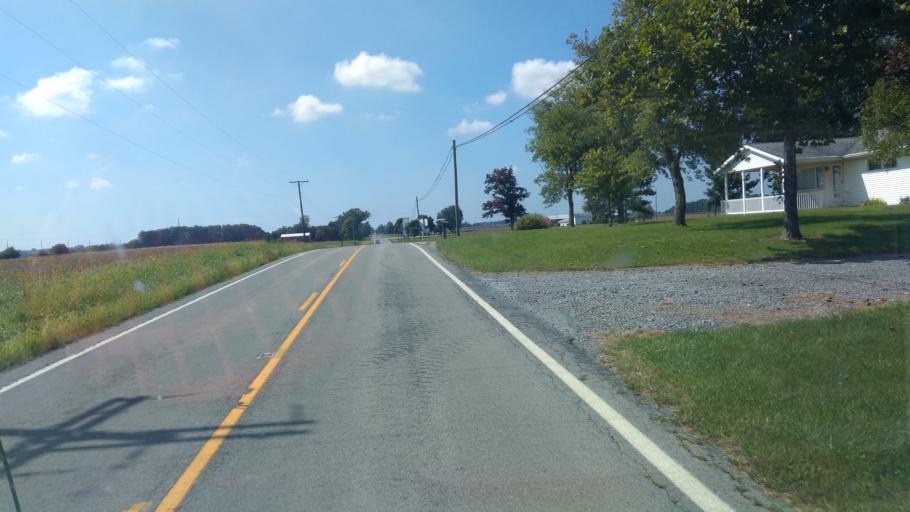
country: US
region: Ohio
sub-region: Hardin County
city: Ada
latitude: 40.7765
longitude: -83.7810
